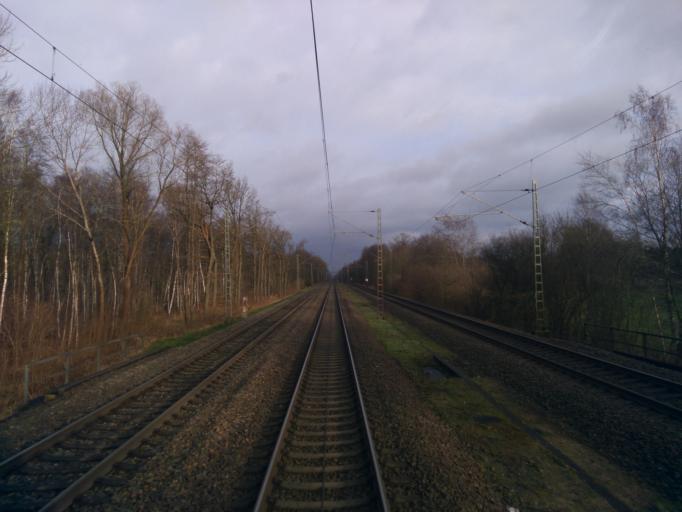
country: DE
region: Lower Saxony
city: Wistedt
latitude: 53.2574
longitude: 9.7003
